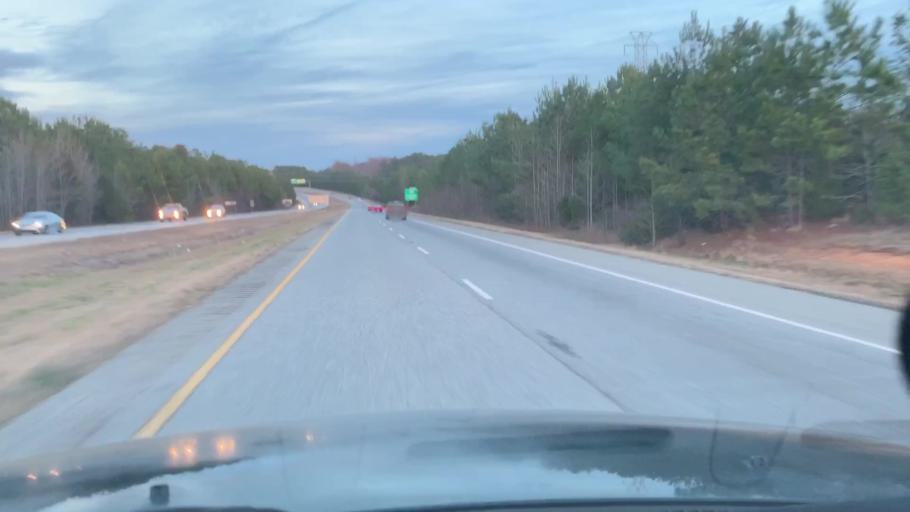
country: US
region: South Carolina
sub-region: Greenville County
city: Mauldin
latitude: 34.7487
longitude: -82.3026
